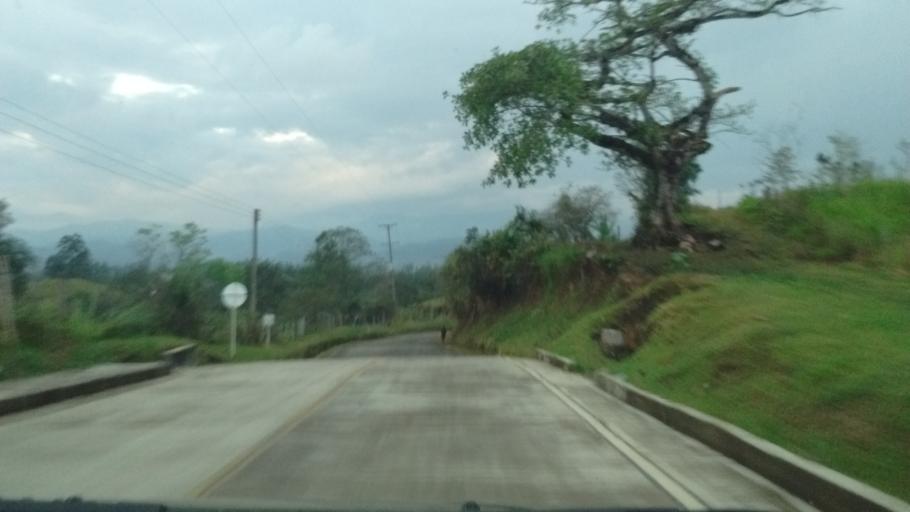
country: CO
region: Cauca
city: Lopez
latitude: 2.3795
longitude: -76.7179
